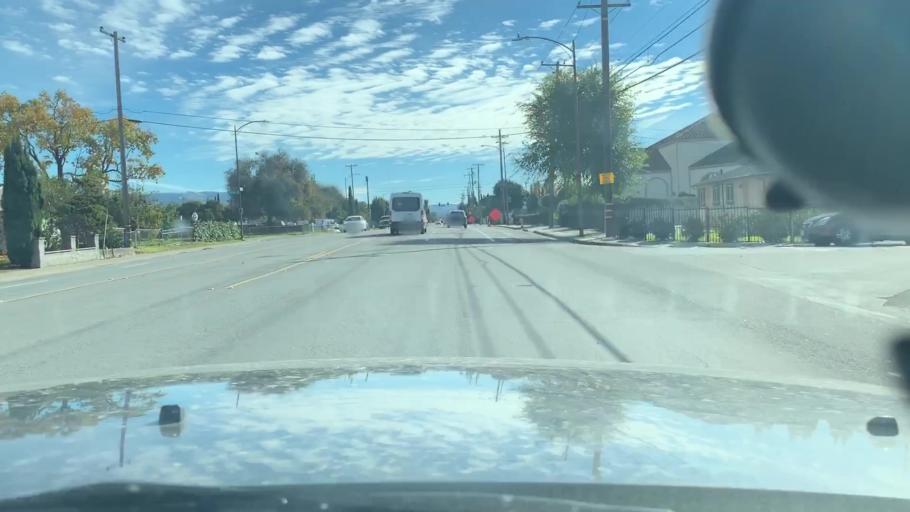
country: US
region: California
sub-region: Santa Clara County
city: Alum Rock
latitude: 37.3527
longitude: -121.8161
